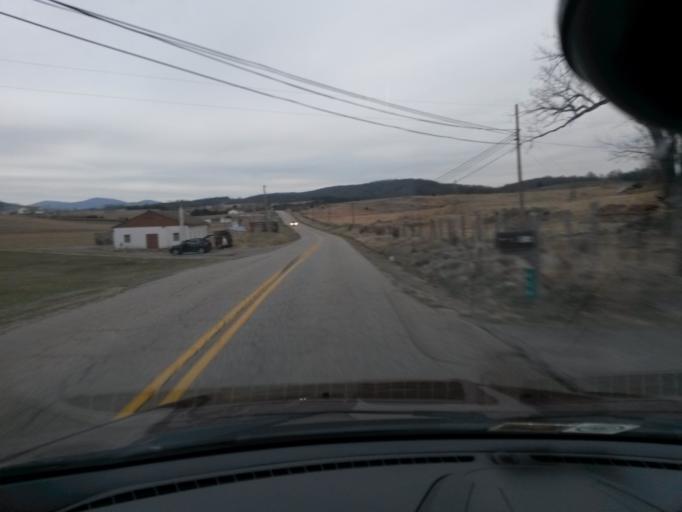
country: US
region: Virginia
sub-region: Rockbridge County
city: East Lexington
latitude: 37.8887
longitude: -79.3711
